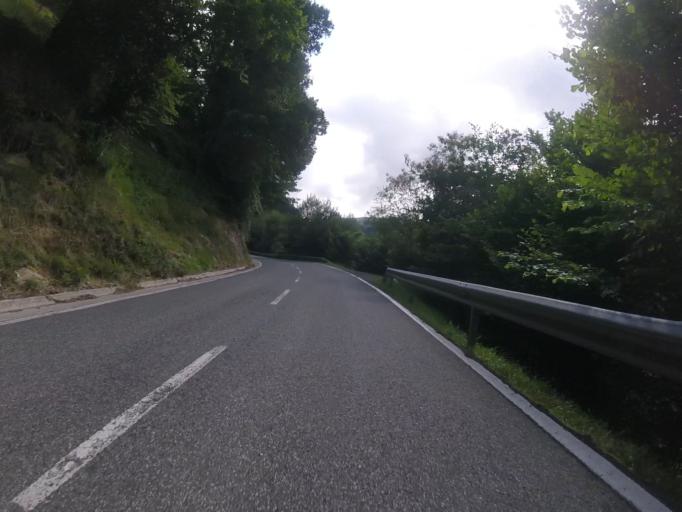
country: ES
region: Navarre
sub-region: Provincia de Navarra
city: Eratsun
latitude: 43.0859
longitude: -1.8020
